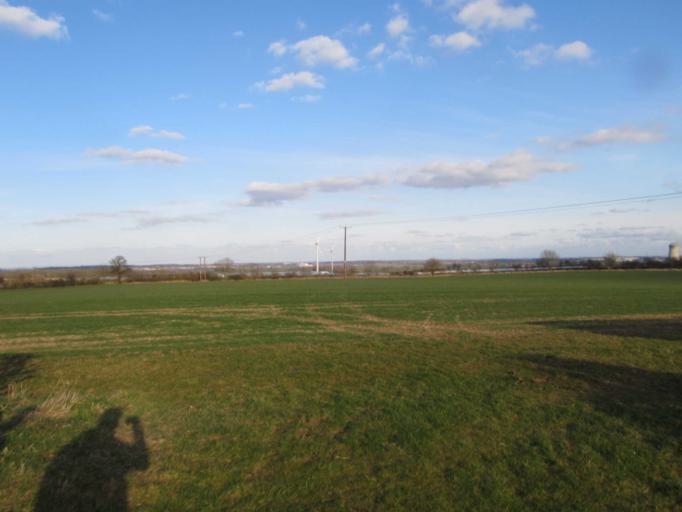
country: GB
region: England
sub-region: Nottinghamshire
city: Misterton
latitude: 53.3800
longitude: -0.8636
